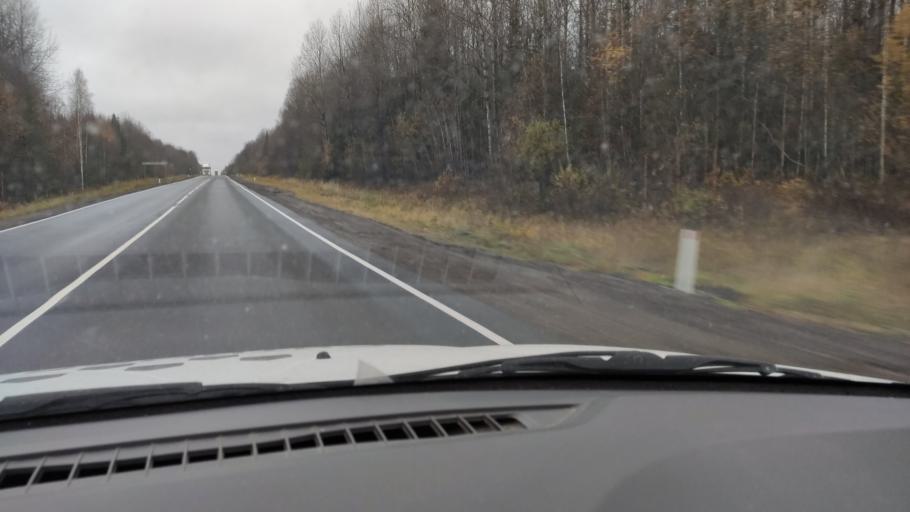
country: RU
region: Kirov
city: Omutninsk
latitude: 58.7560
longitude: 52.0353
